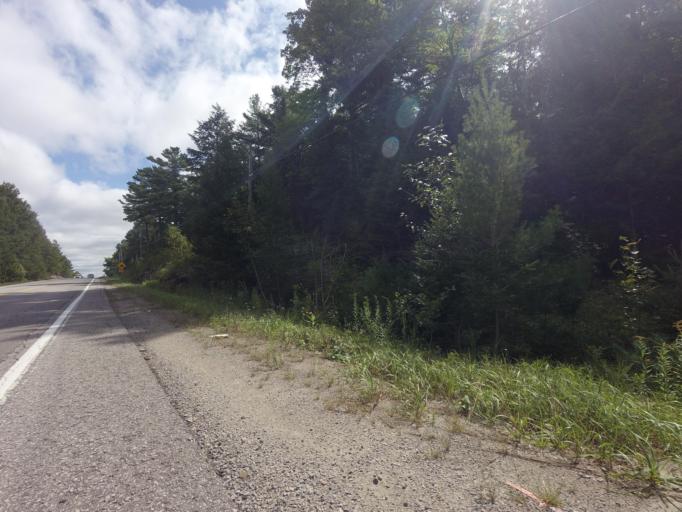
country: CA
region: Ontario
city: Omemee
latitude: 44.8044
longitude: -78.6106
